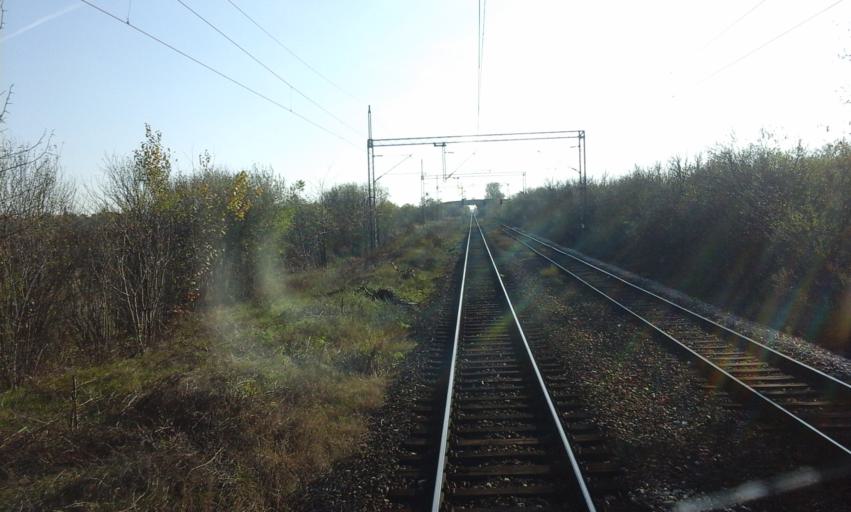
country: RS
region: Autonomna Pokrajina Vojvodina
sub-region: Severnobacki Okrug
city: Mali Igos
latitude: 45.7454
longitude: 19.6490
